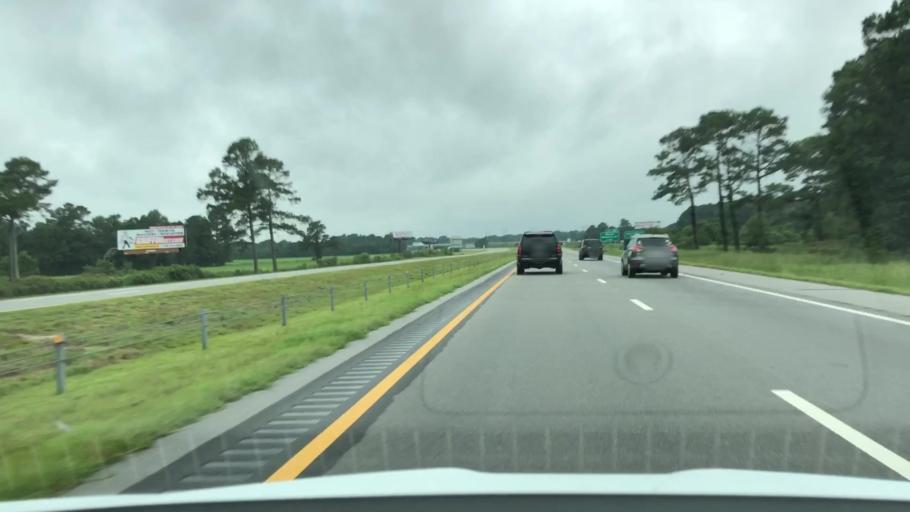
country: US
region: North Carolina
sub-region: Wayne County
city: Elroy
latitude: 35.4161
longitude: -77.9086
